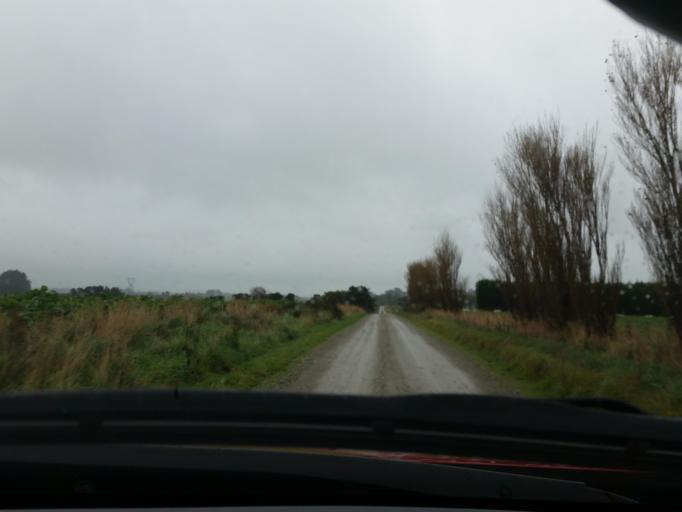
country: NZ
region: Southland
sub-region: Invercargill City
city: Invercargill
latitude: -46.3310
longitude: 168.4425
